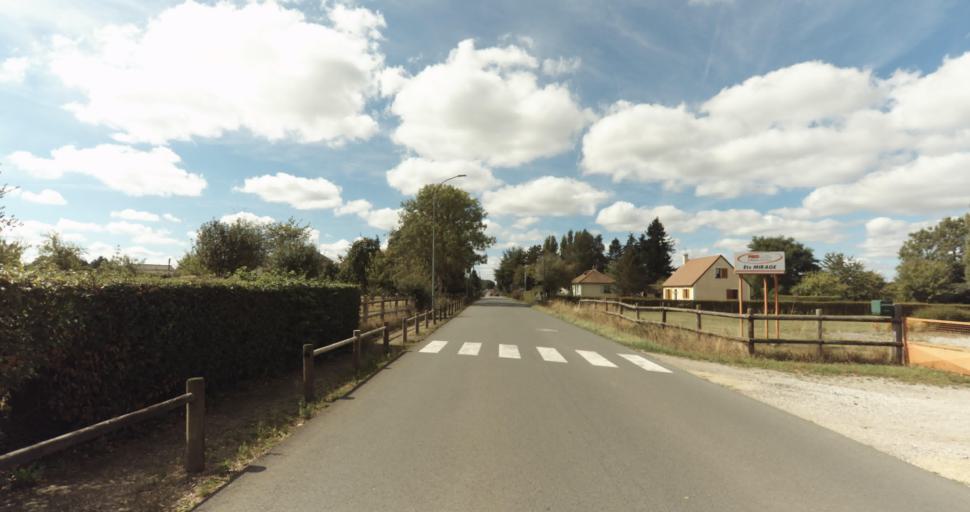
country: FR
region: Lower Normandy
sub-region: Departement de l'Orne
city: Gace
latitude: 48.8949
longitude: 0.3457
